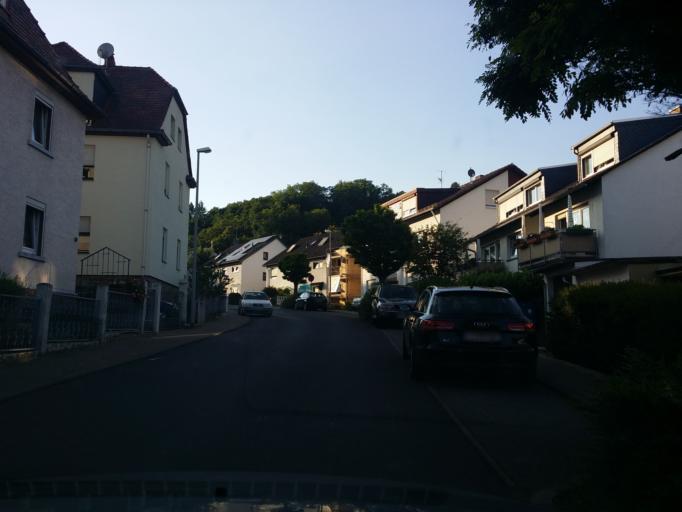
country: DE
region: Hesse
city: Eppstein
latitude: 50.1427
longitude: 8.3954
